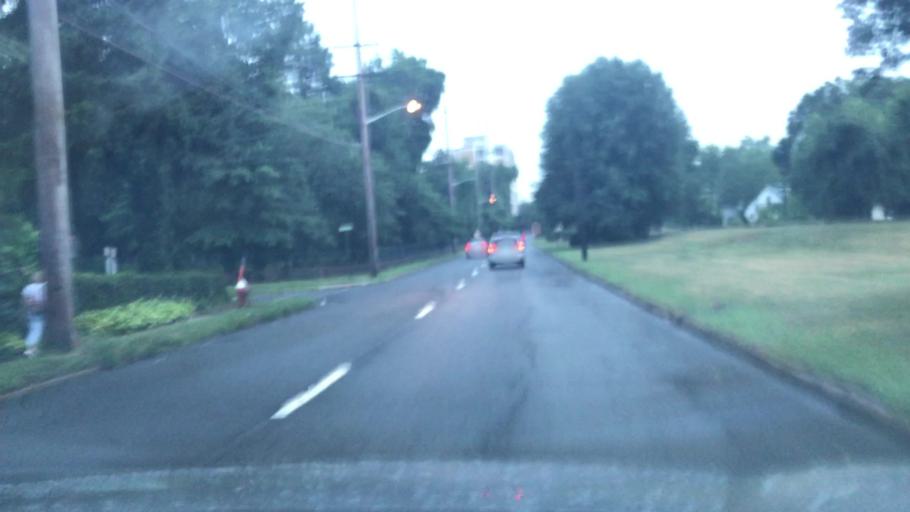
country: US
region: New Jersey
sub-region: Bergen County
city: Englewood
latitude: 40.9092
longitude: -73.9683
